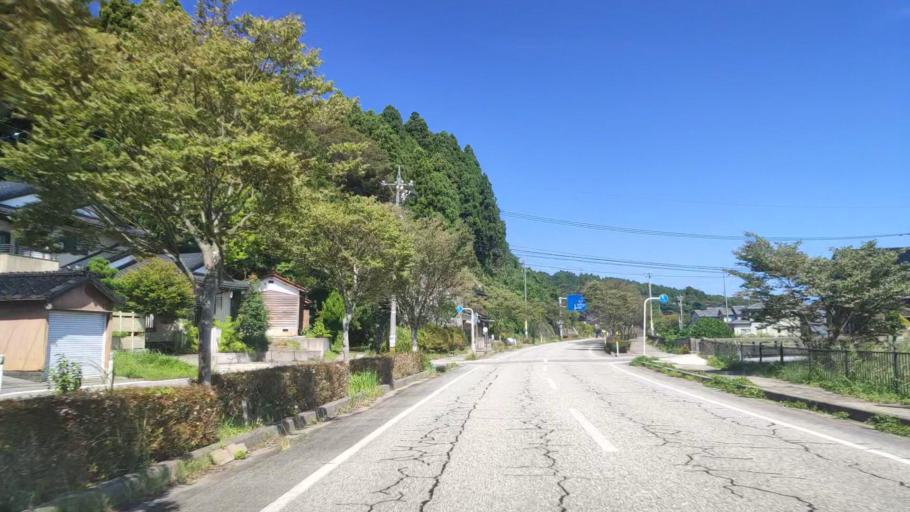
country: JP
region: Ishikawa
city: Nanao
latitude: 37.3913
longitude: 136.8926
